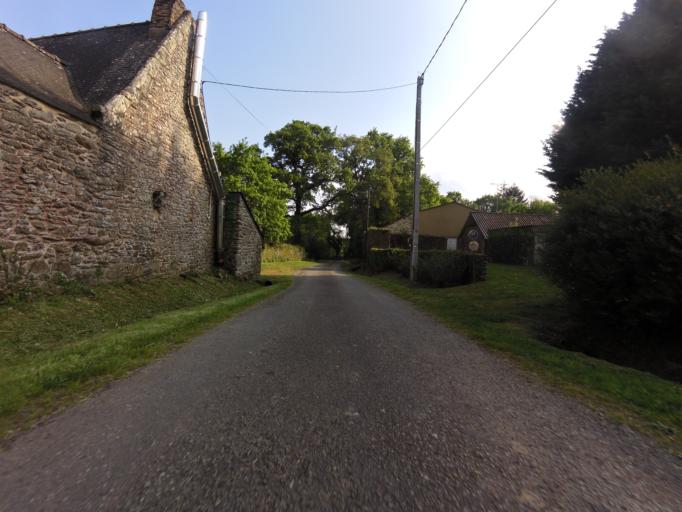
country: FR
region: Brittany
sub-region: Departement du Morbihan
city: Pluherlin
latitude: 47.7205
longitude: -2.3767
